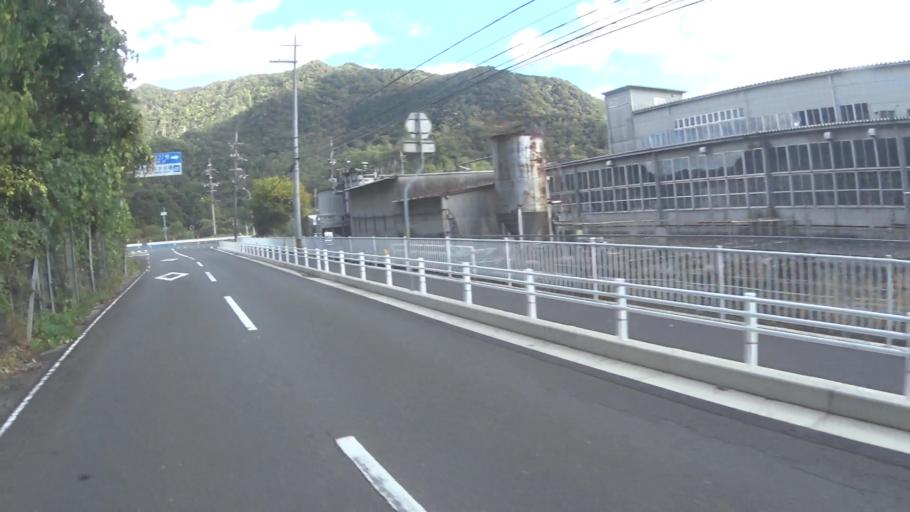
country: JP
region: Kyoto
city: Maizuru
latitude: 35.5156
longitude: 135.4005
